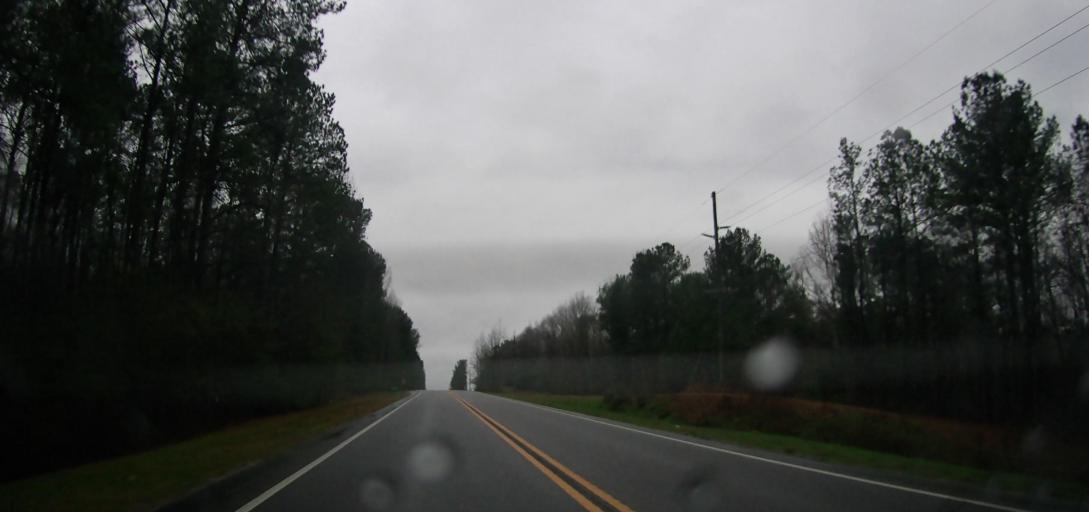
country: US
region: Alabama
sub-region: Bibb County
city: West Blocton
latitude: 33.0874
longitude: -87.1372
